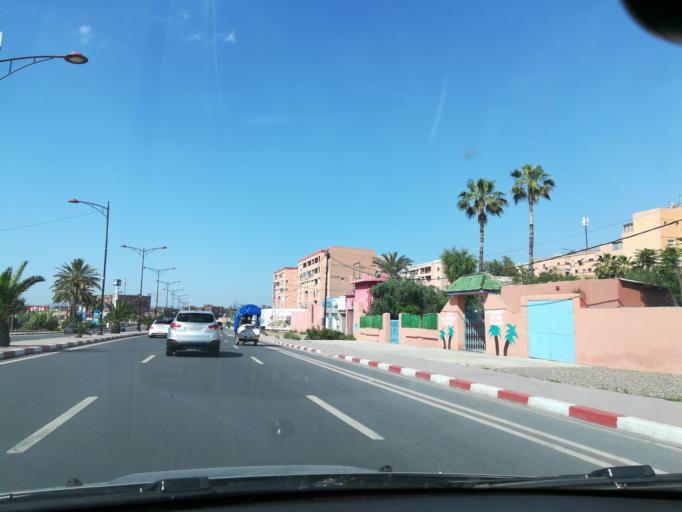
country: MA
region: Marrakech-Tensift-Al Haouz
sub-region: Marrakech
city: Marrakesh
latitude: 31.6650
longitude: -8.0126
